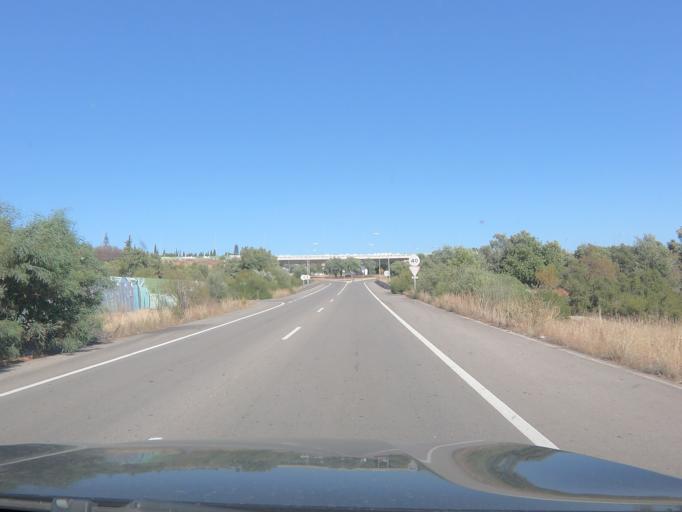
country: PT
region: Faro
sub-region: Loule
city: Almancil
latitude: 37.1057
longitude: -8.0480
